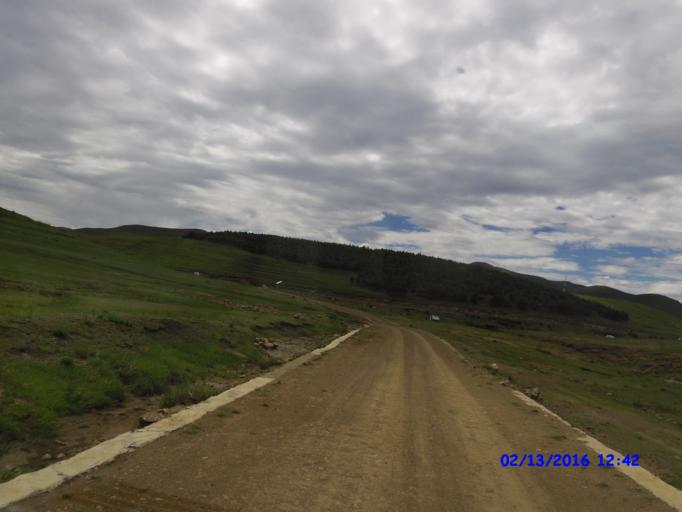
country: LS
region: Maseru
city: Nako
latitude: -29.8291
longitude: 28.0360
